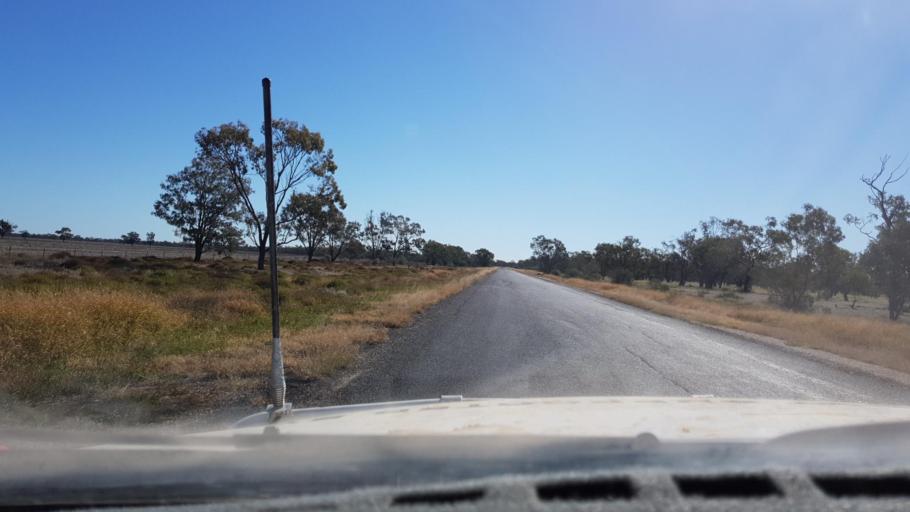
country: AU
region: New South Wales
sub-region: Walgett
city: Lightning Ridge
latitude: -29.5747
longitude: 148.6738
